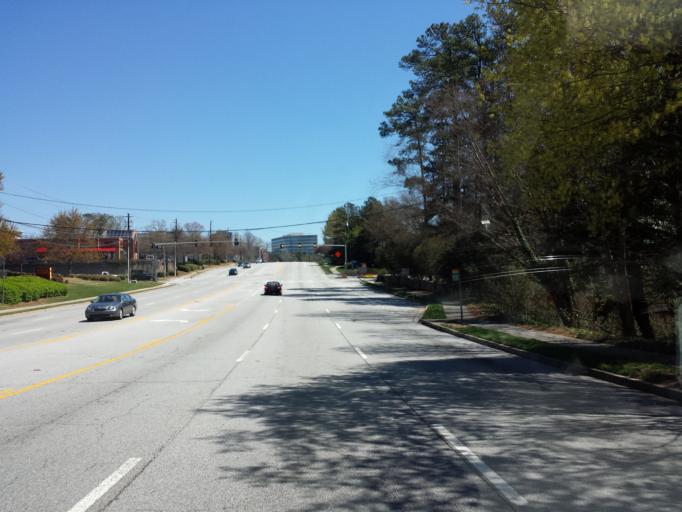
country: US
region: Georgia
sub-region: Fulton County
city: Sandy Springs
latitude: 33.9189
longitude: -84.3548
